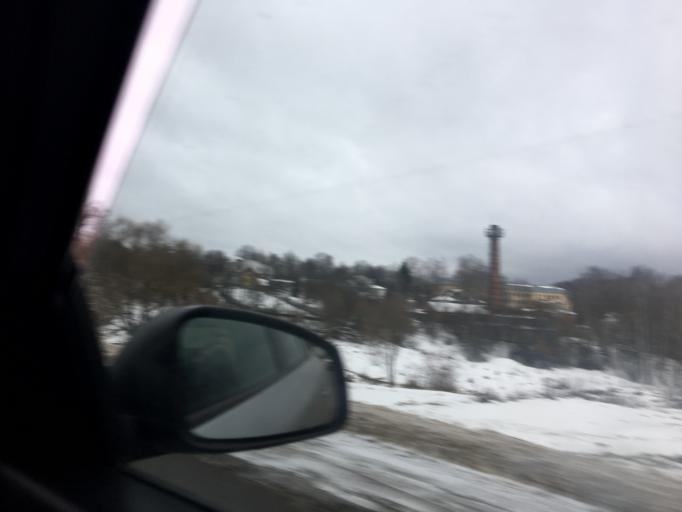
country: RU
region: Tula
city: Pervomayskiy
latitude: 54.0747
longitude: 37.5410
